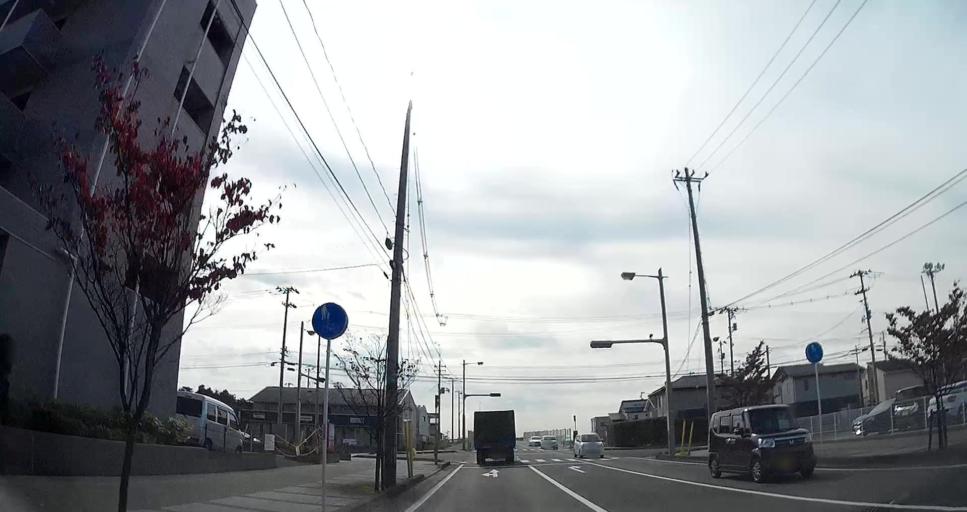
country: JP
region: Miyagi
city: Iwanuma
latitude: 38.1568
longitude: 140.9195
